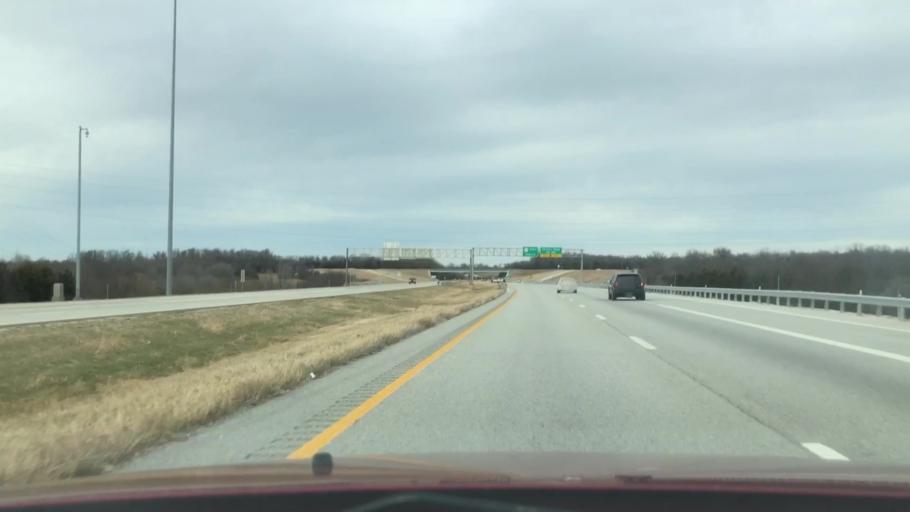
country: US
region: Missouri
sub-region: Greene County
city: Springfield
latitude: 37.2540
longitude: -93.2243
